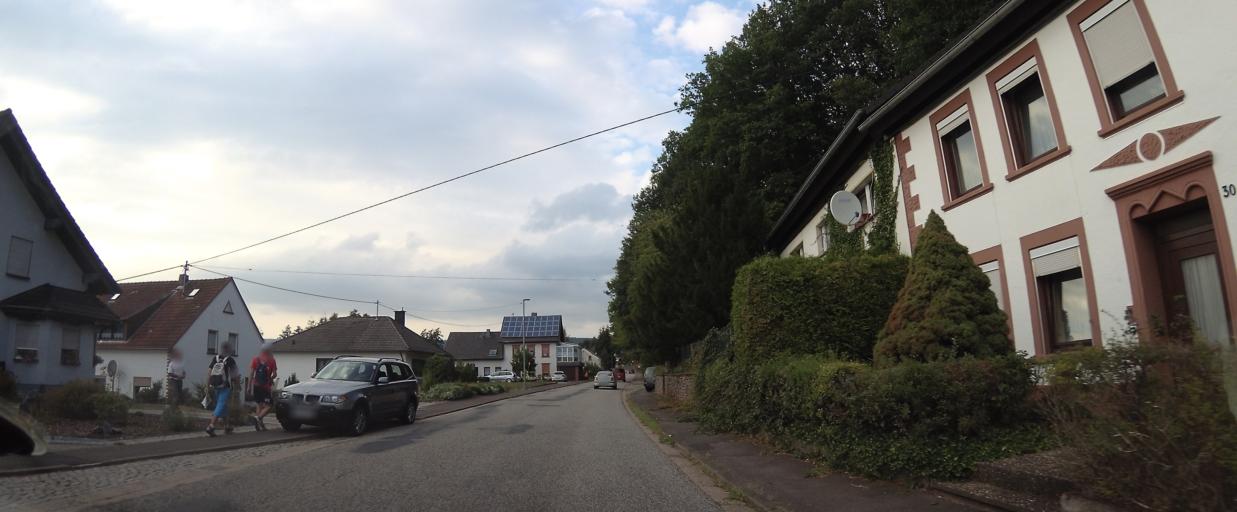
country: DE
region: Saarland
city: Wadern
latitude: 49.5553
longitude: 6.8643
